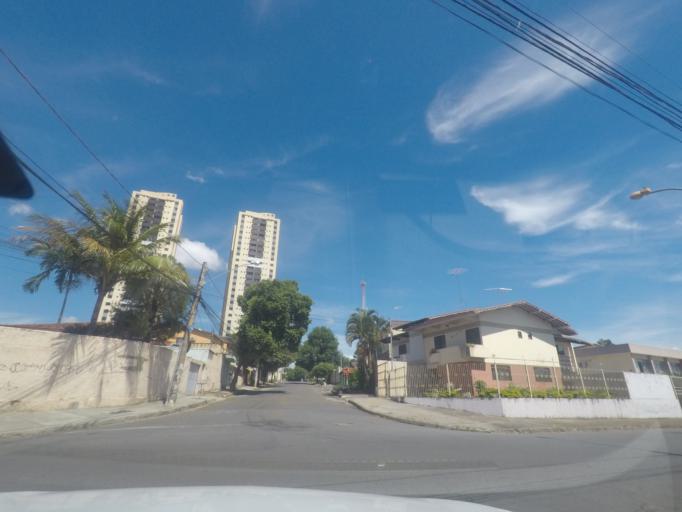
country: BR
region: Goias
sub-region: Goiania
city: Goiania
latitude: -16.6720
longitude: -49.2766
